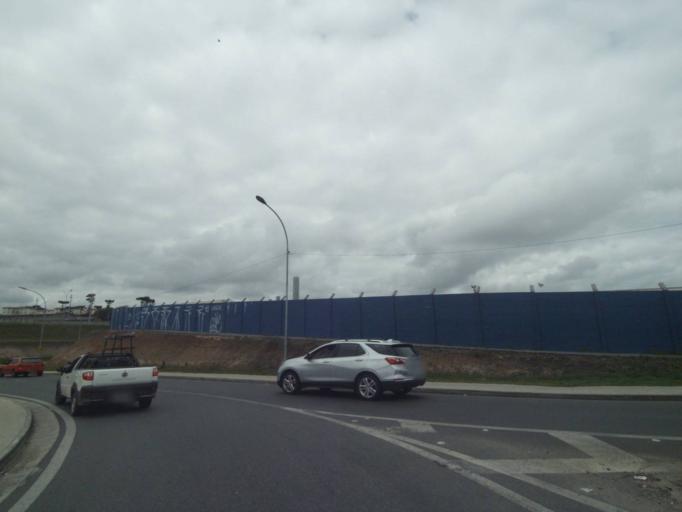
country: BR
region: Parana
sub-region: Pinhais
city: Pinhais
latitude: -25.3901
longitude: -49.1900
